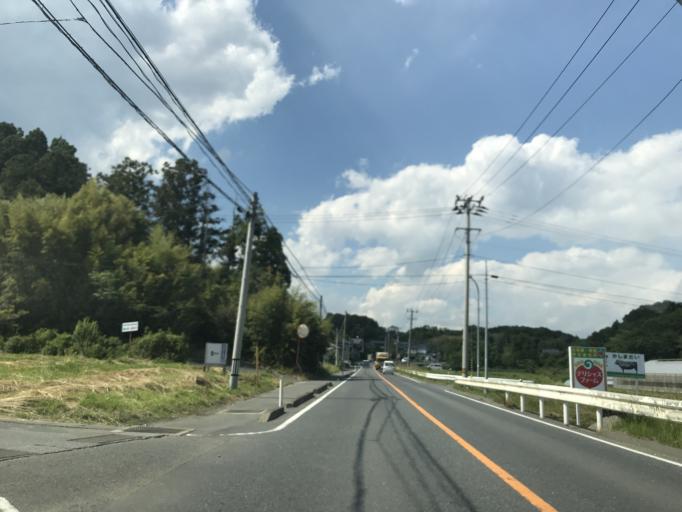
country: JP
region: Miyagi
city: Wakuya
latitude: 38.4867
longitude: 141.1078
